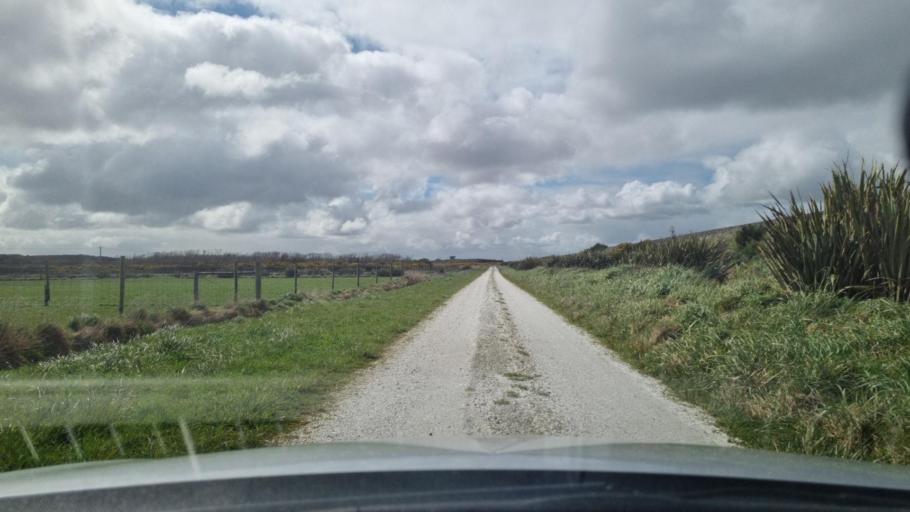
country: NZ
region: Southland
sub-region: Invercargill City
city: Bluff
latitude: -46.5336
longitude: 168.3045
